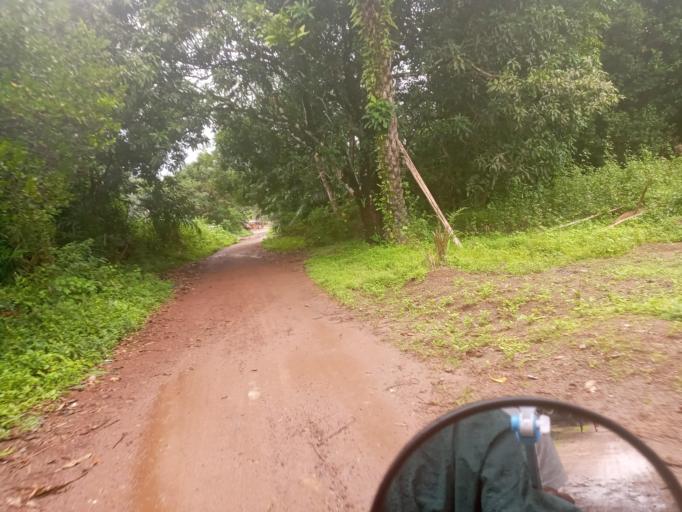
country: SL
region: Northern Province
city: Bumbuna
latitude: 8.9450
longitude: -11.7508
